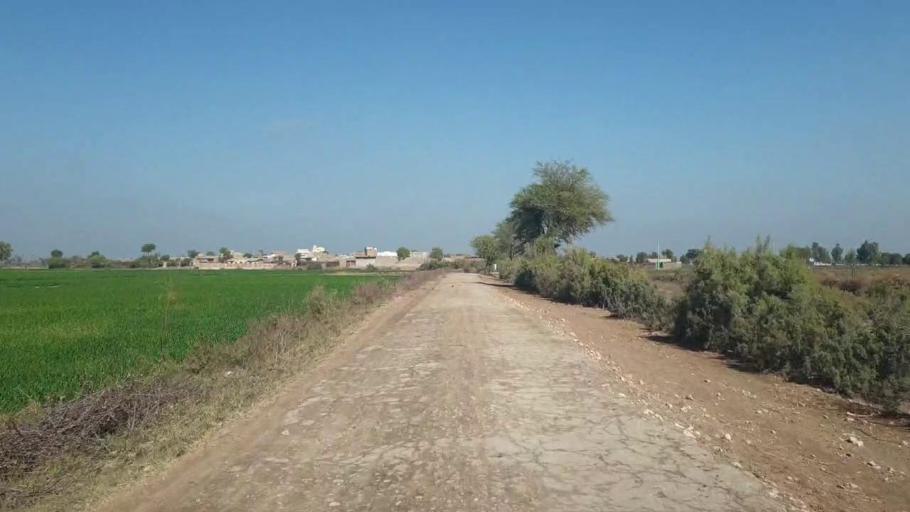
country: PK
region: Sindh
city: Bhit Shah
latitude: 25.8815
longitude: 68.5261
